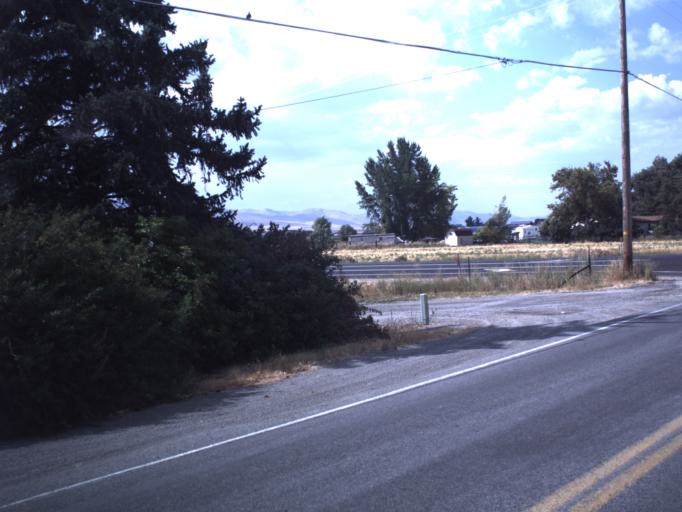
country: US
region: Utah
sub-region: Box Elder County
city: Garland
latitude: 41.7850
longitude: -112.1251
